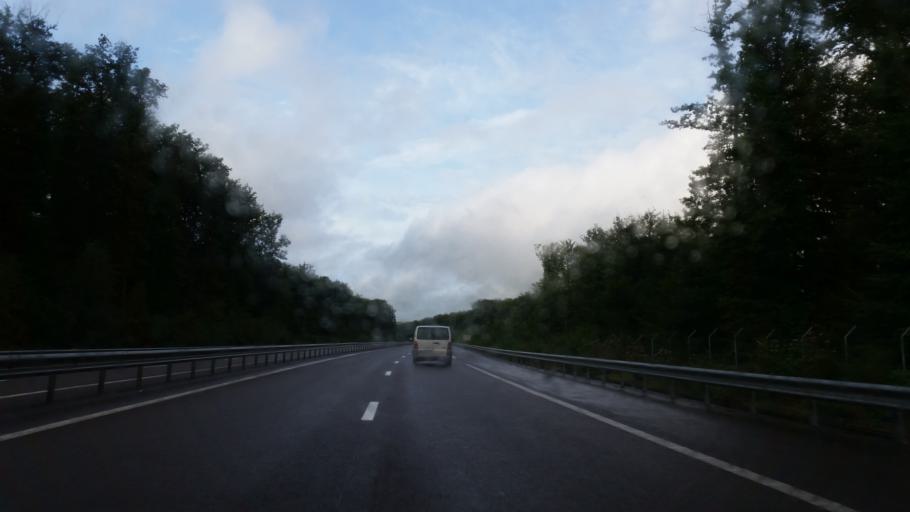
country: FR
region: Franche-Comte
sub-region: Departement de la Haute-Saone
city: Froideconche
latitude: 47.8249
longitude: 6.3963
